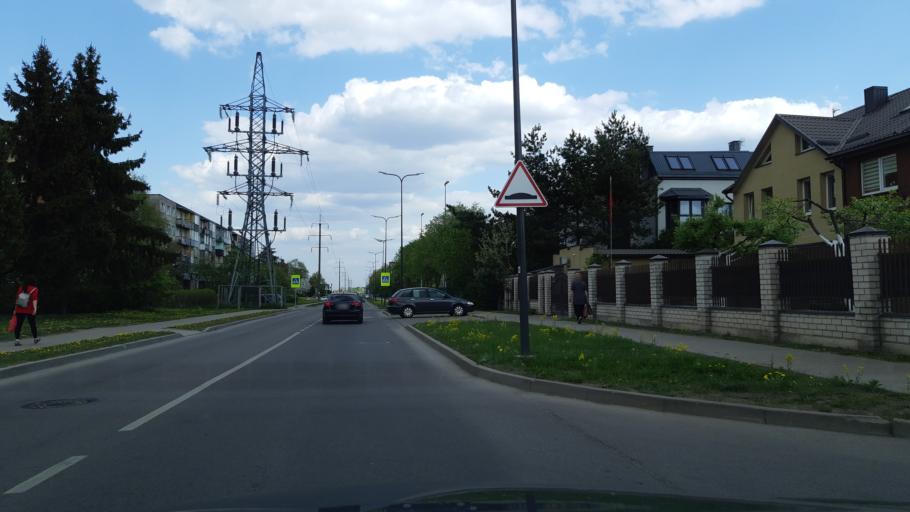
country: LT
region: Kauno apskritis
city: Dainava (Kaunas)
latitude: 54.9238
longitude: 23.9682
